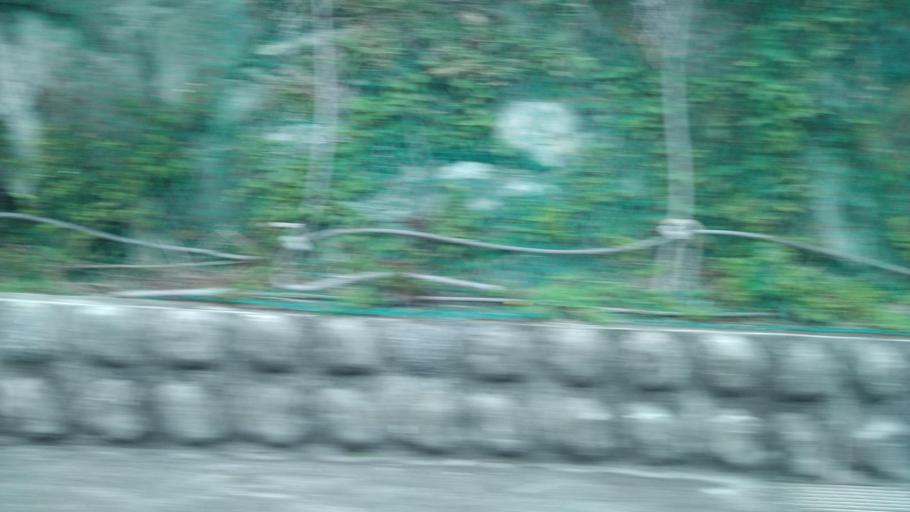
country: TW
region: Taiwan
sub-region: Hualien
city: Hualian
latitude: 24.2268
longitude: 121.7054
